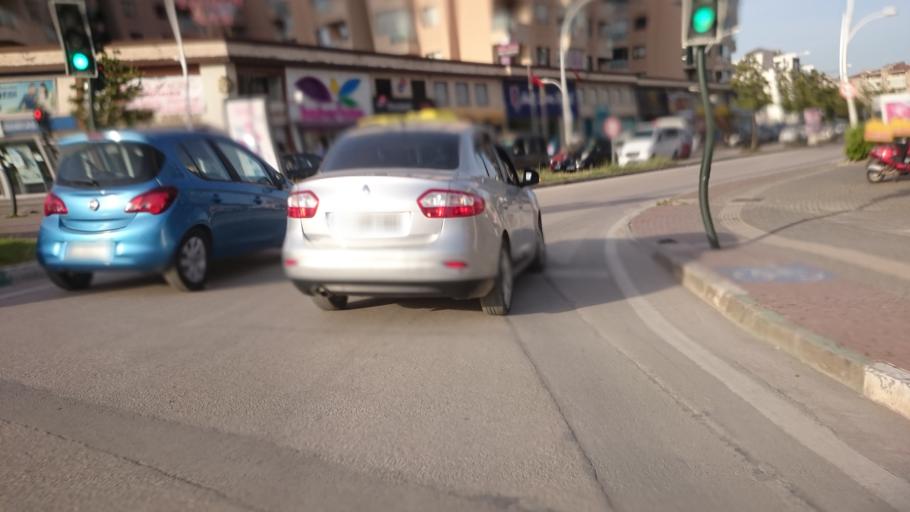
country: TR
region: Bursa
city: Cali
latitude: 40.2206
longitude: 28.9150
